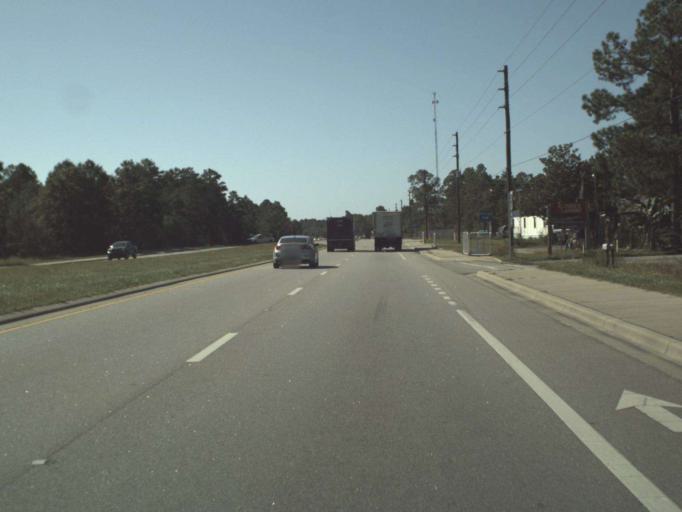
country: US
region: Florida
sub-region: Walton County
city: Seaside
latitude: 30.3817
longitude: -86.1774
